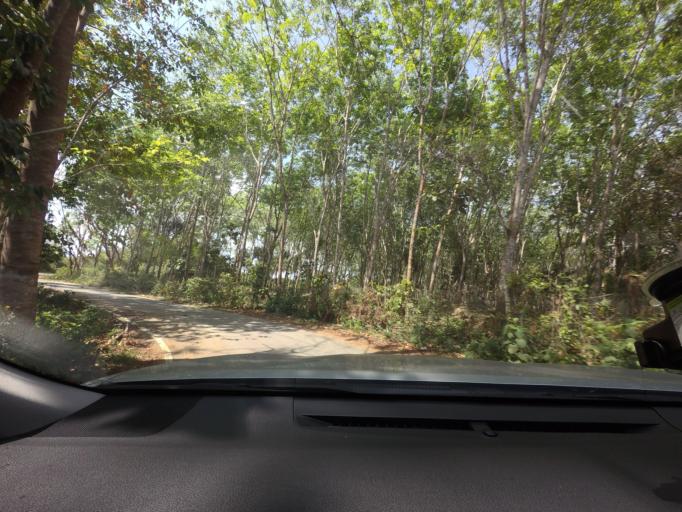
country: TH
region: Narathiwat
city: Rueso
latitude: 6.3785
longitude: 101.5065
